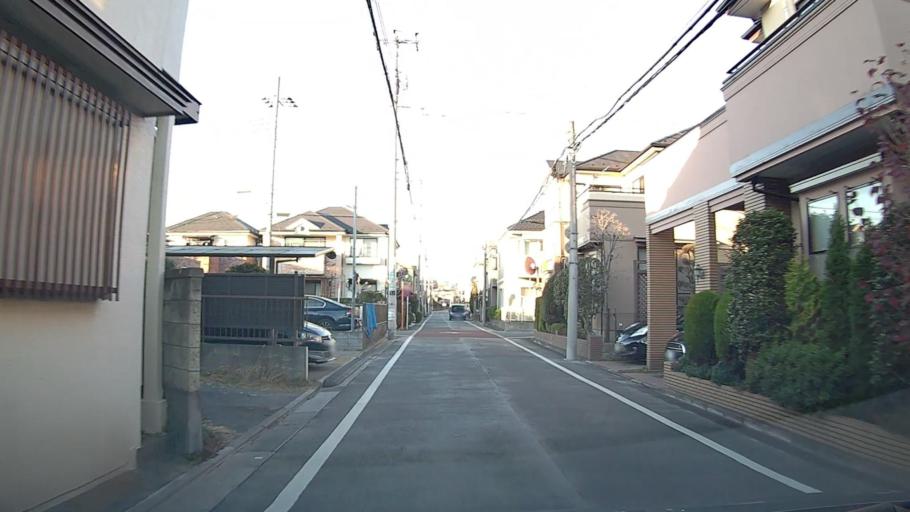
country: JP
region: Saitama
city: Wako
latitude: 35.7628
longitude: 139.6417
